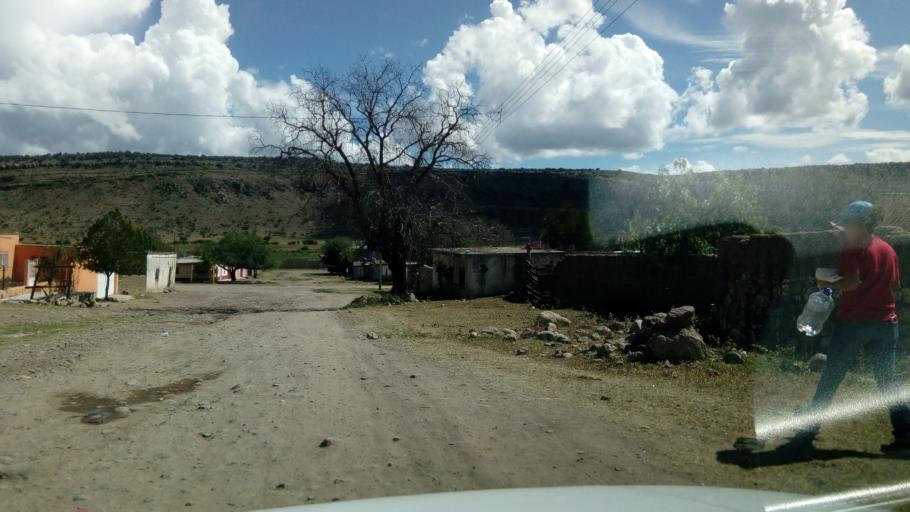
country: MX
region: Durango
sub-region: Durango
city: Jose Refugio Salcido
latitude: 23.7930
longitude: -104.4875
